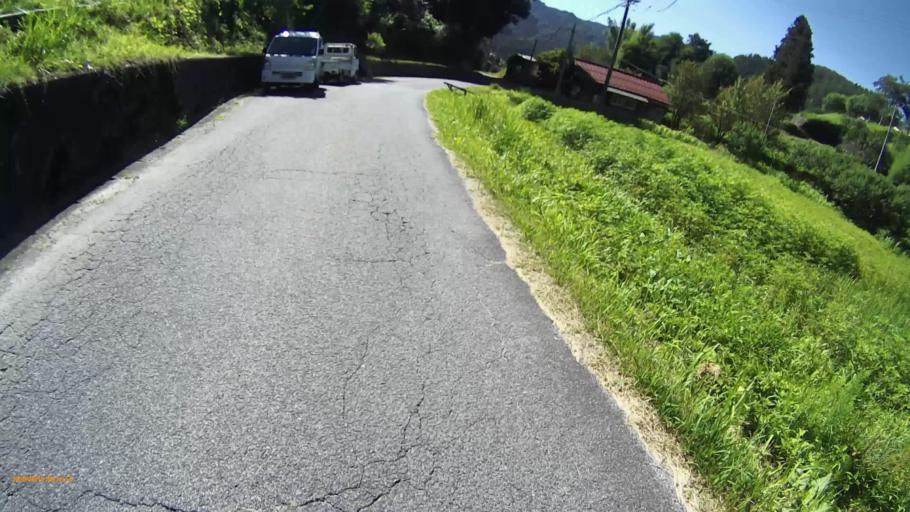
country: JP
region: Nagano
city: Iida
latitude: 35.6889
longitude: 137.6733
